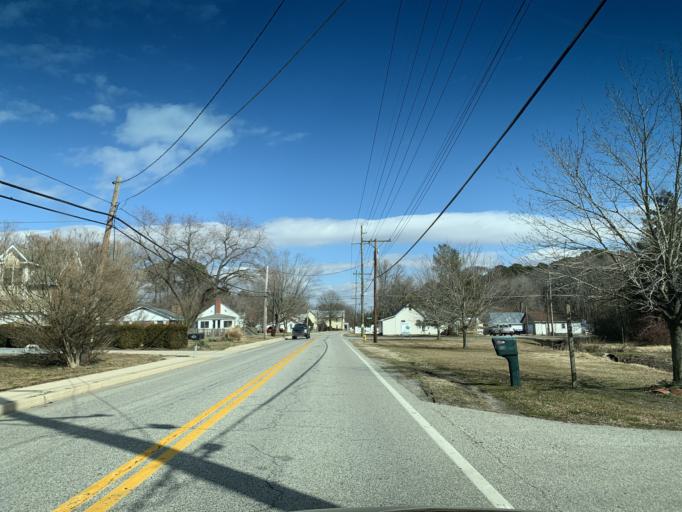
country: US
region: Maryland
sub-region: Queen Anne's County
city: Grasonville
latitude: 38.9594
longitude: -76.1993
